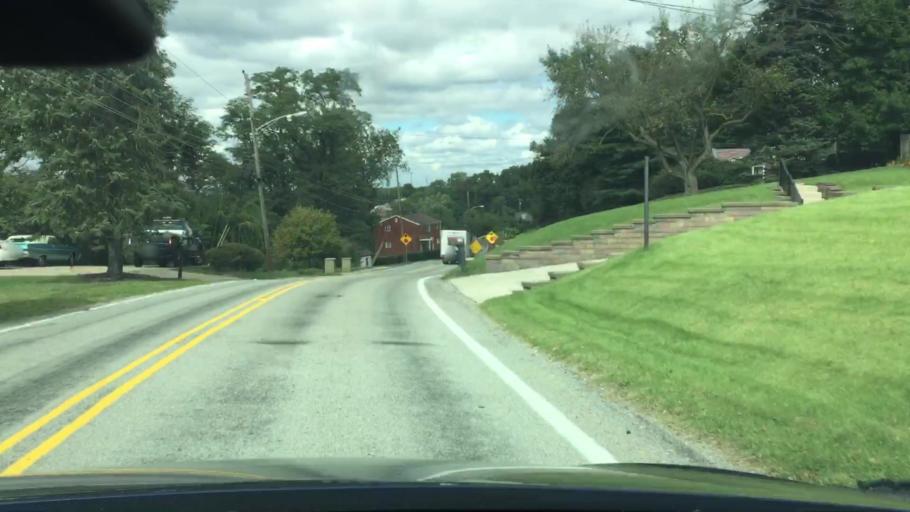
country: US
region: Pennsylvania
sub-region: Allegheny County
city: Penn Hills
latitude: 40.4858
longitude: -79.8206
